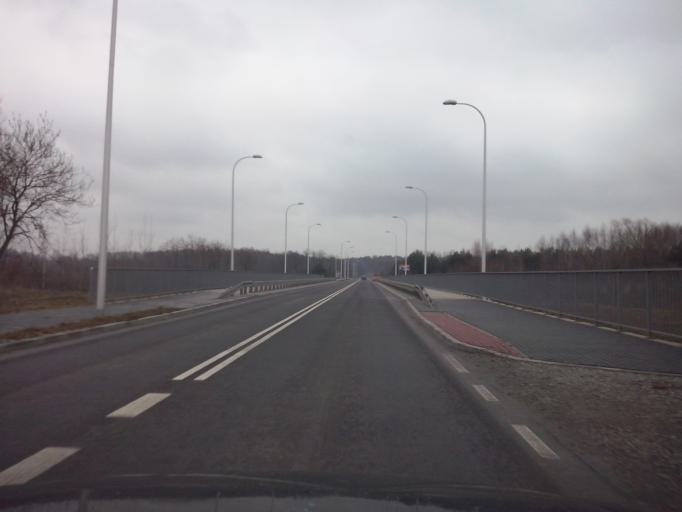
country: PL
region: Subcarpathian Voivodeship
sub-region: Powiat nizanski
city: Przedzel
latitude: 50.5175
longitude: 22.2270
